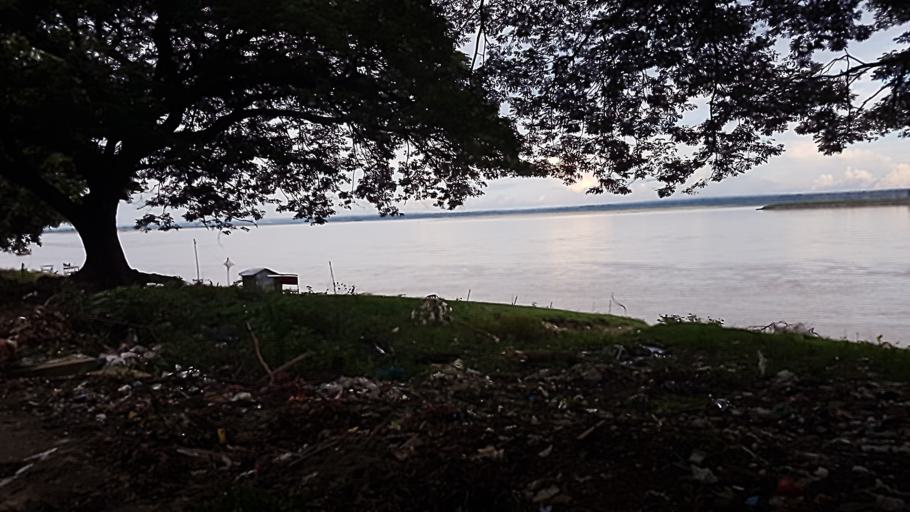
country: MM
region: Magway
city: Minbu
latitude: 20.1739
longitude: 94.8801
